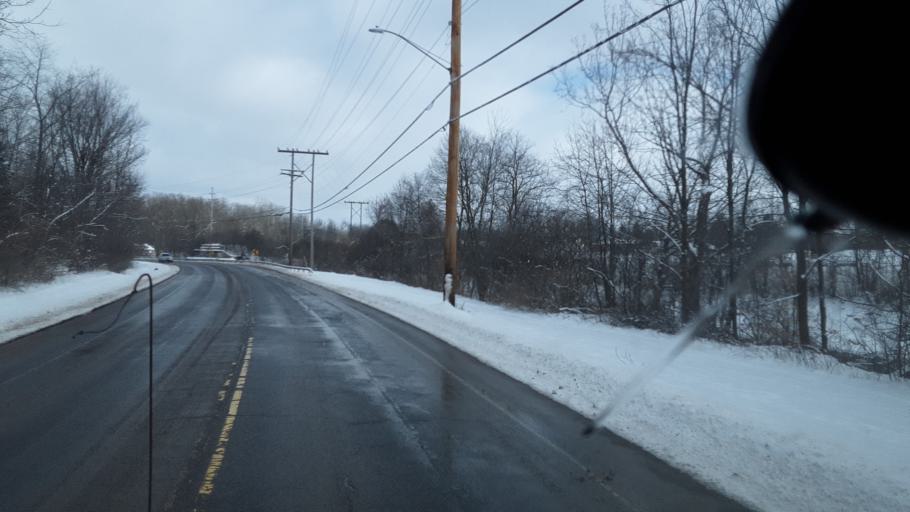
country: US
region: New York
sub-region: Wayne County
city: Newark
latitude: 43.0473
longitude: -77.0794
